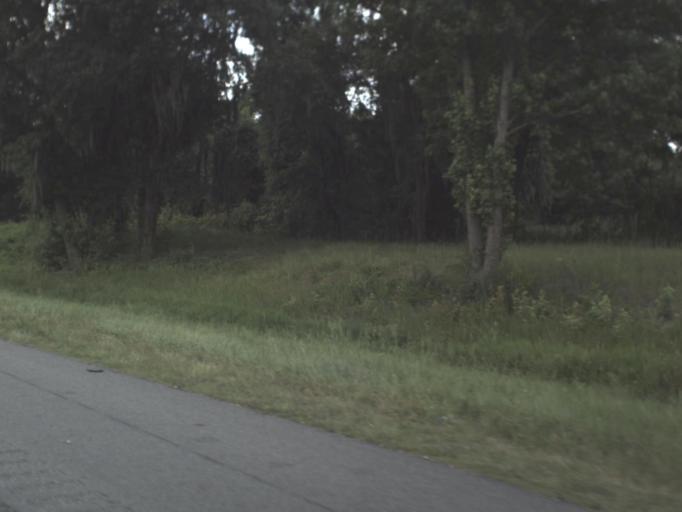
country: US
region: Florida
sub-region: Hamilton County
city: Jasper
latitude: 30.3961
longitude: -82.8815
